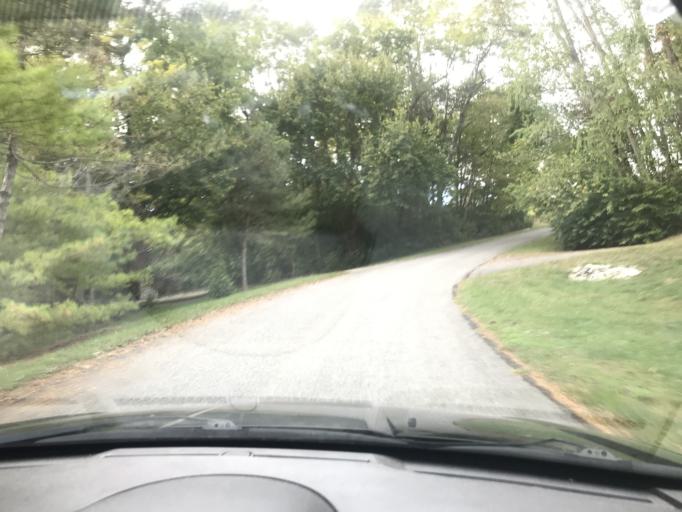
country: US
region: Ohio
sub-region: Logan County
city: West Liberty
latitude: 40.2588
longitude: -83.7104
